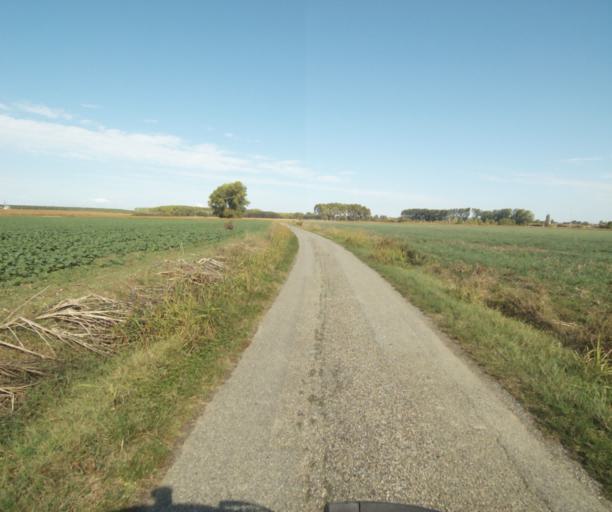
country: FR
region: Midi-Pyrenees
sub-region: Departement du Tarn-et-Garonne
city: Finhan
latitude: 43.8924
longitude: 1.2208
